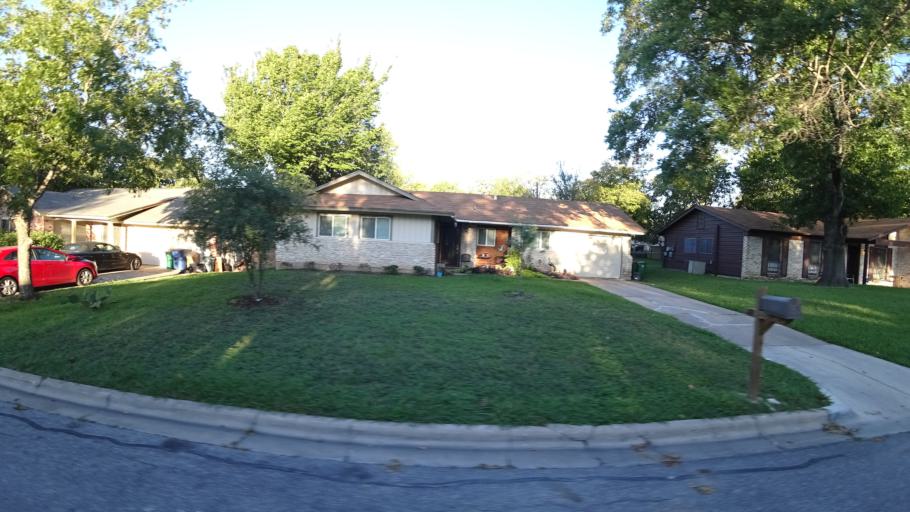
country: US
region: Texas
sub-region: Travis County
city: Austin
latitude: 30.2964
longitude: -97.6767
